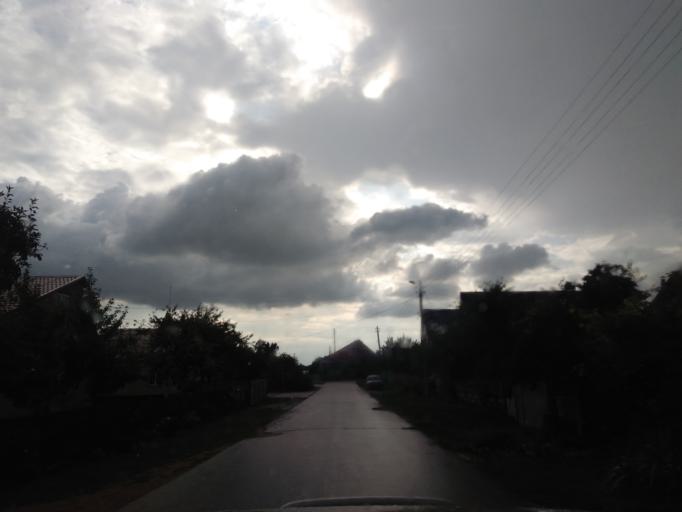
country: BY
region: Minsk
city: Kapyl'
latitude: 53.1449
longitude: 27.1128
